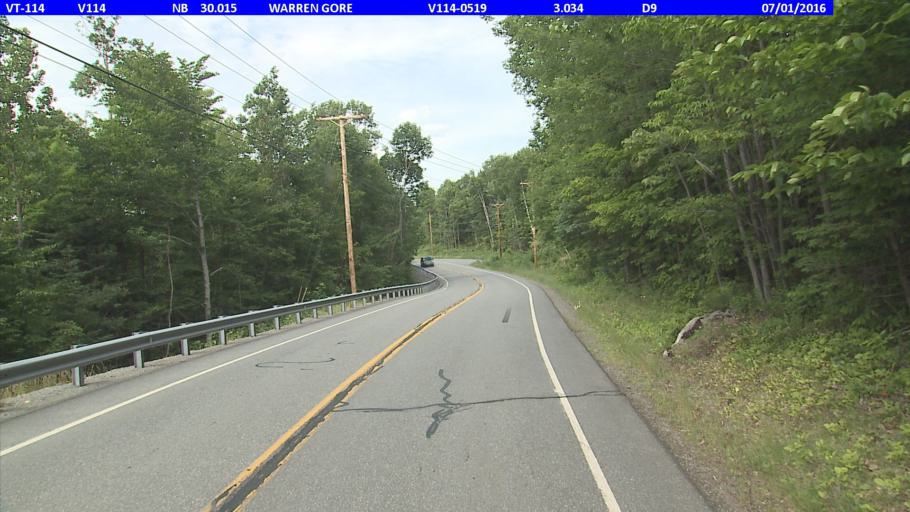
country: CA
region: Quebec
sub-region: Estrie
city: Coaticook
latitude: 44.9262
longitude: -71.8690
